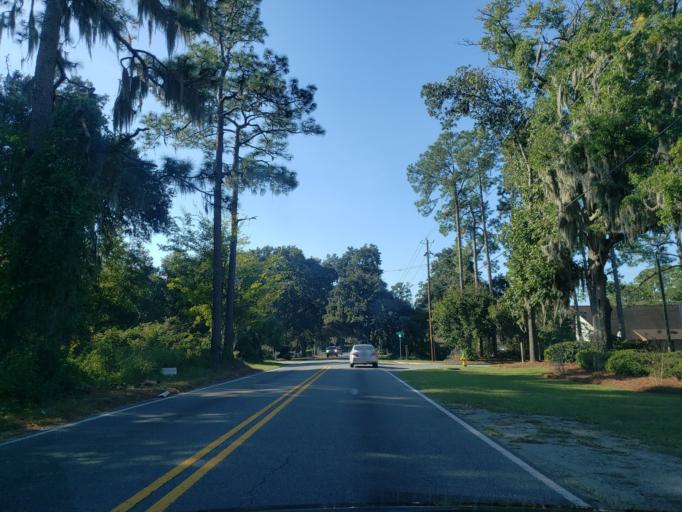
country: US
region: Georgia
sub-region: Chatham County
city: Thunderbolt
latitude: 32.0156
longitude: -81.0770
